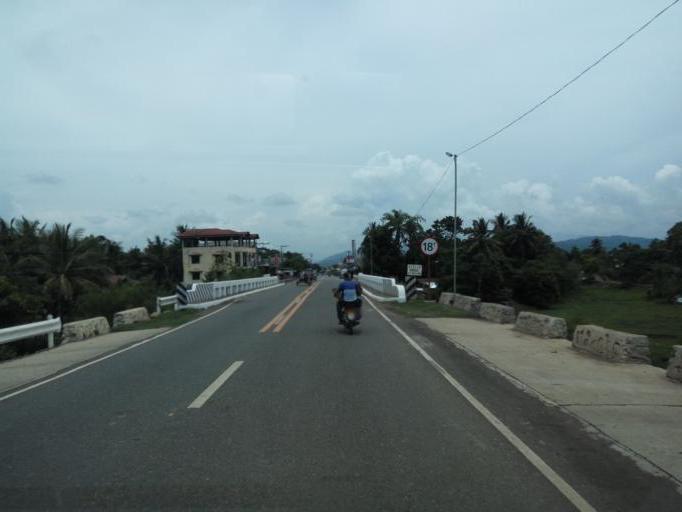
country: PH
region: Cagayan Valley
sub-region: Province of Quirino
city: Saguday
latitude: 16.5207
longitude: 121.5219
